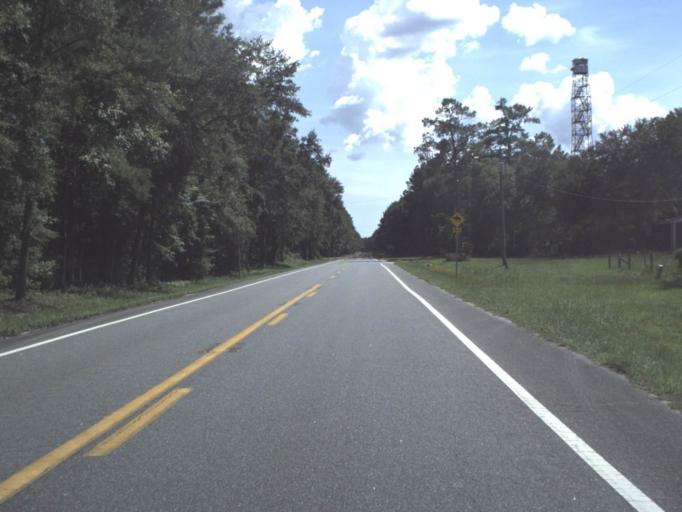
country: US
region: Florida
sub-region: Lafayette County
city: Mayo
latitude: 29.9287
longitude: -83.2775
